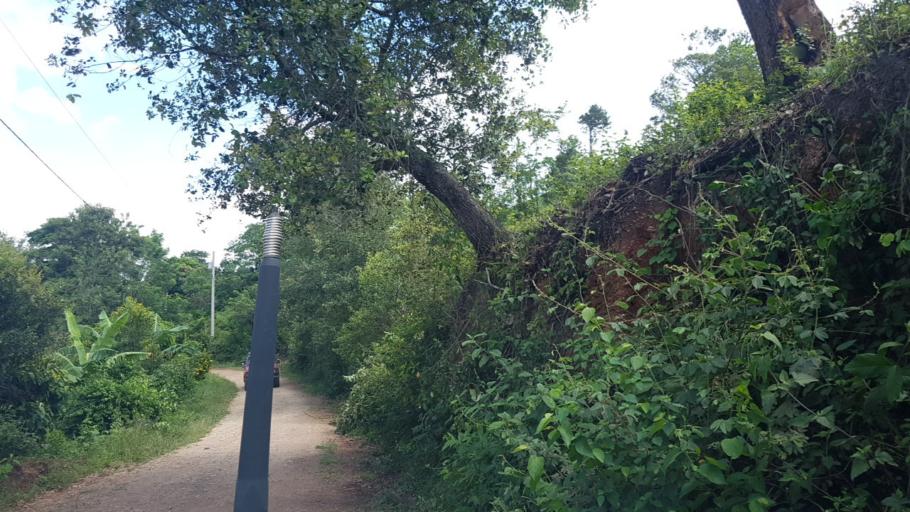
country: NI
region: Nueva Segovia
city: Ciudad Antigua
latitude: 13.6513
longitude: -86.2473
